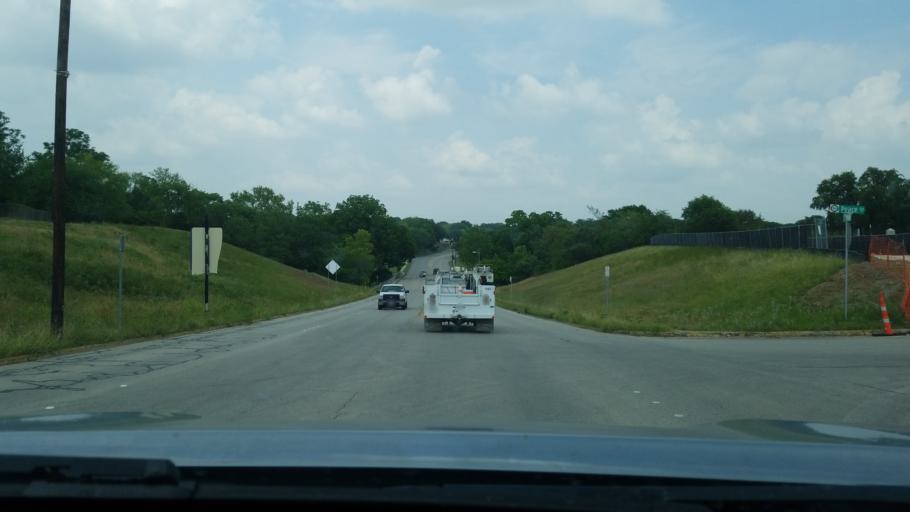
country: US
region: Texas
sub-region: Comal County
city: New Braunfels
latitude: 29.7144
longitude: -98.1111
